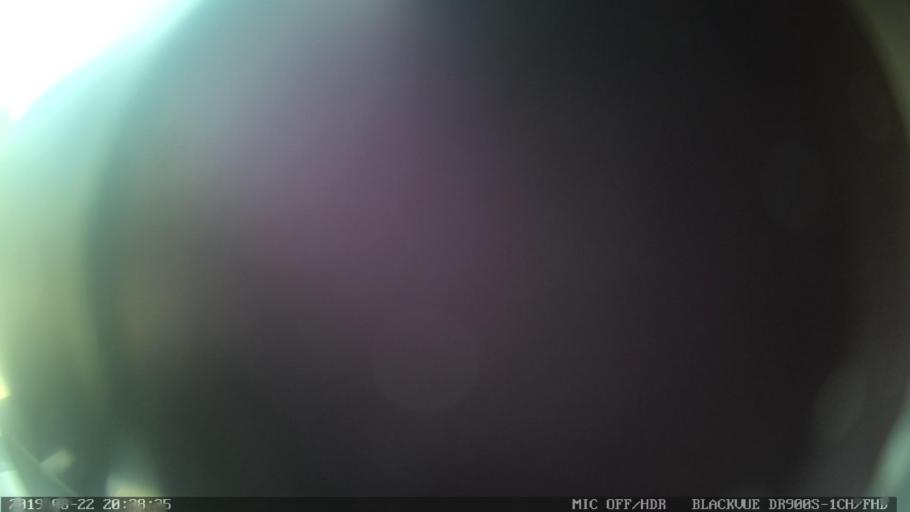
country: PT
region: Castelo Branco
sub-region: Proenca-A-Nova
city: Proenca-a-Nova
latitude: 39.6873
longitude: -7.7506
